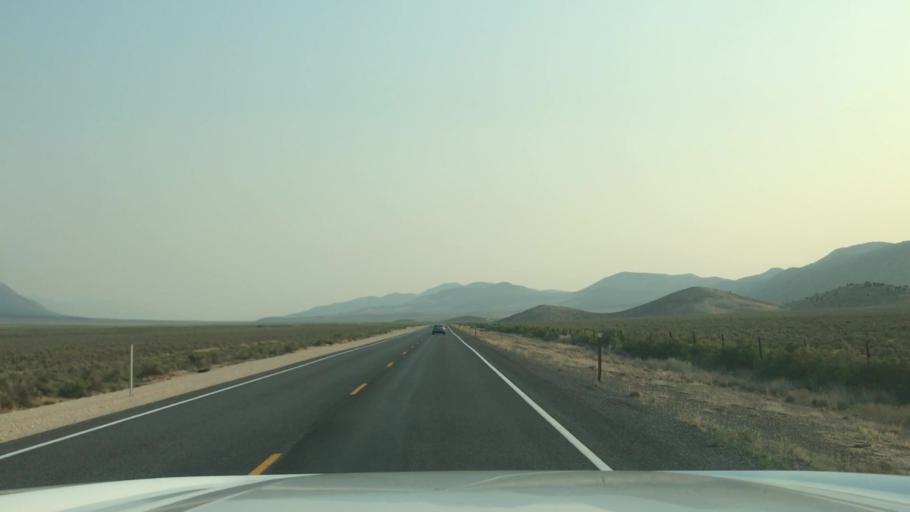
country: US
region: Utah
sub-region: Sevier County
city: Aurora
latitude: 39.0691
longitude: -112.0421
